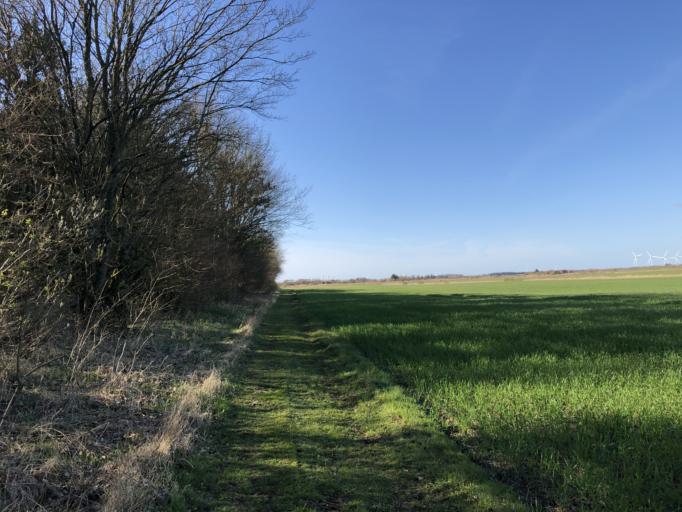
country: DK
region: Central Jutland
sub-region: Holstebro Kommune
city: Ulfborg
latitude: 56.3266
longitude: 8.3186
